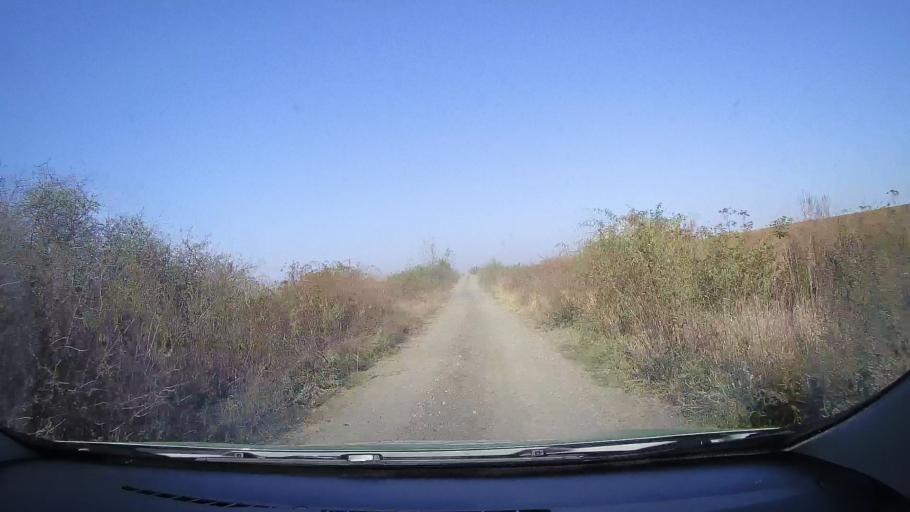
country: RO
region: Satu Mare
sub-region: Comuna Sauca
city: Sauca
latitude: 47.4808
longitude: 22.4689
